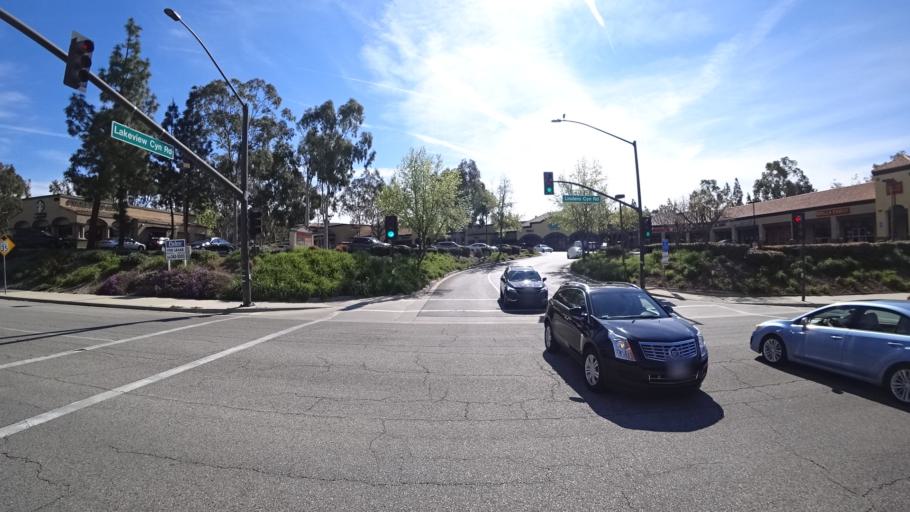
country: US
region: California
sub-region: Ventura County
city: Oak Park
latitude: 34.1831
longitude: -118.7862
